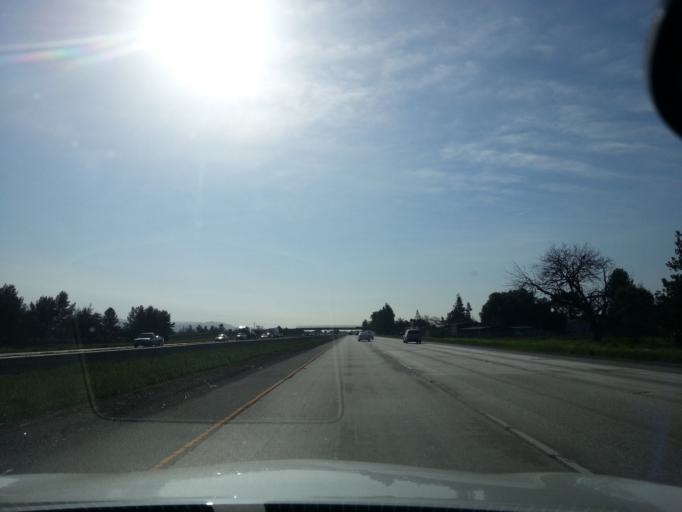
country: US
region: California
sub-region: Santa Clara County
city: Morgan Hill
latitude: 37.1451
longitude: -121.6451
